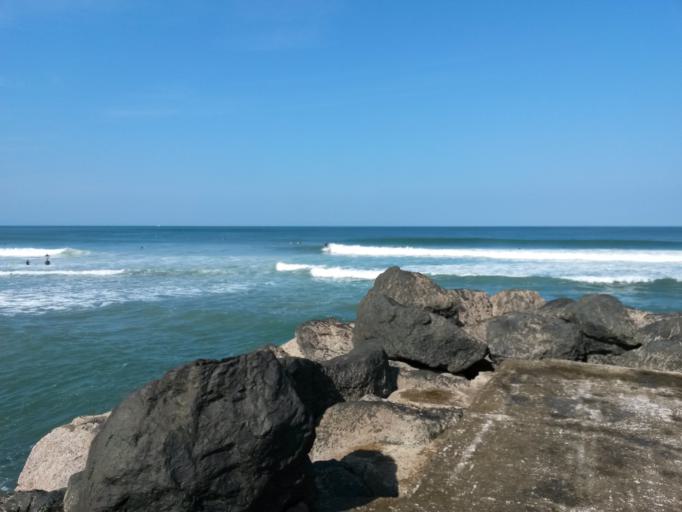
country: FR
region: Aquitaine
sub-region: Departement des Pyrenees-Atlantiques
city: Biarritz
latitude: 43.5065
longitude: -1.5395
